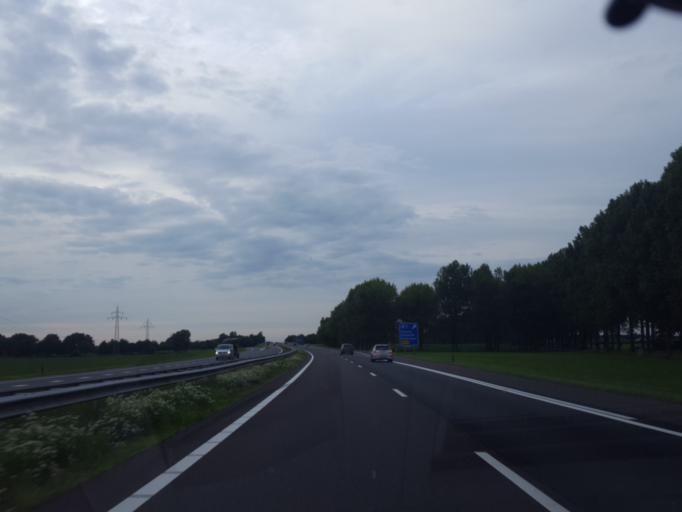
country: NL
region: Drenthe
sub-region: Gemeente Meppel
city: Meppel
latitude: 52.7218
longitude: 6.2049
